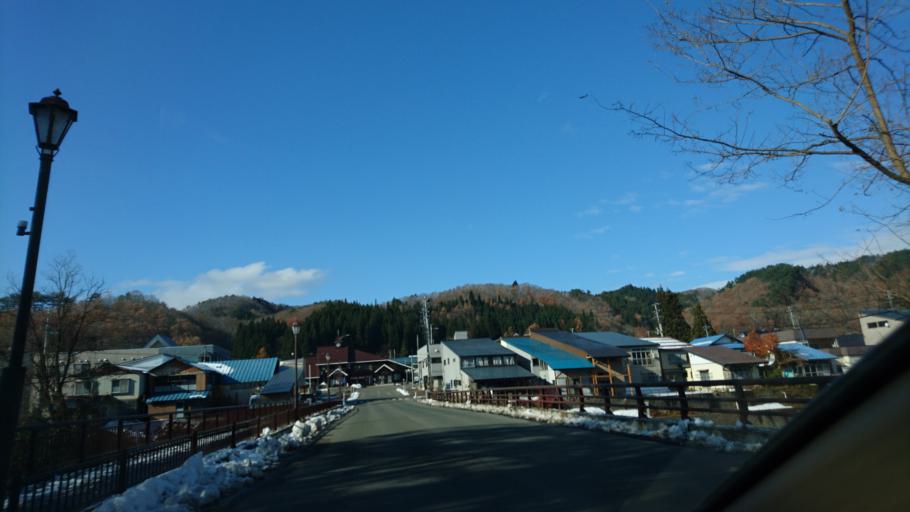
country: JP
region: Akita
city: Yokotemachi
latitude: 39.3138
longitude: 140.7774
